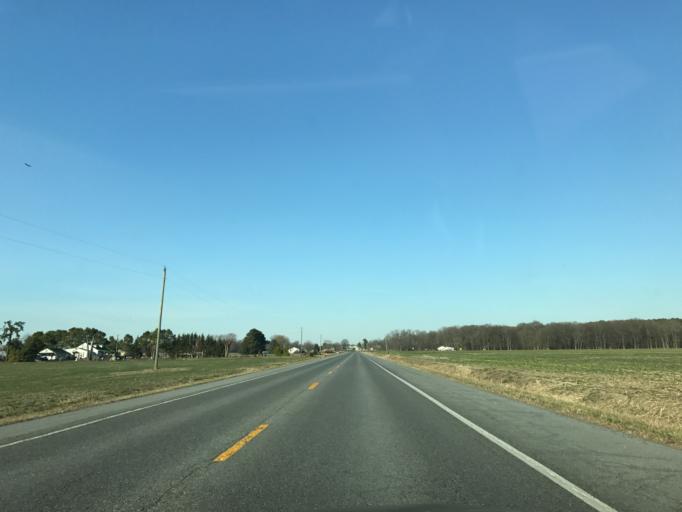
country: US
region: Maryland
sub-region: Caroline County
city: Greensboro
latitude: 39.1292
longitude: -75.8659
